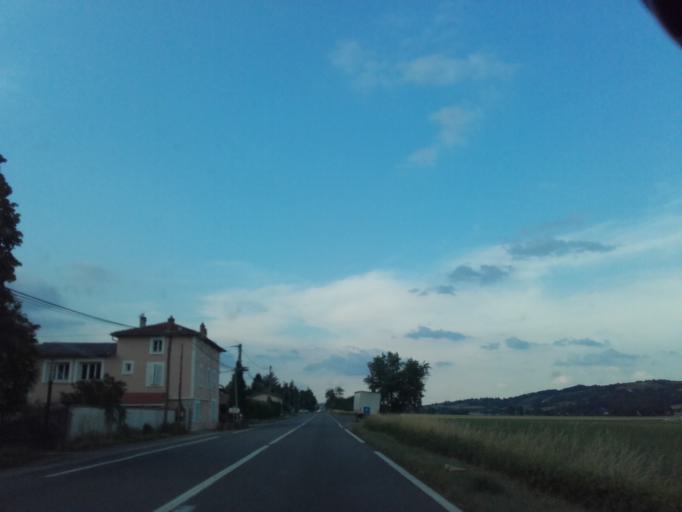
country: FR
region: Rhone-Alpes
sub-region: Departement de l'Isere
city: Reventin-Vaugris
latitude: 45.4624
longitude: 4.8261
